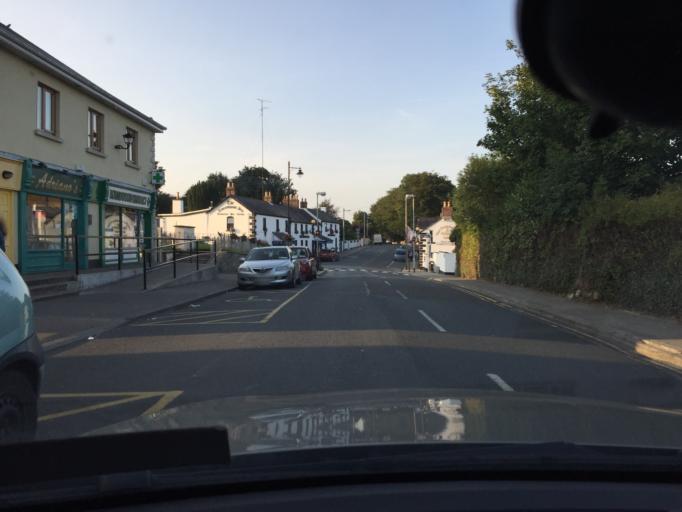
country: IE
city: Newtownmountkennedy
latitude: 53.0638
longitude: -6.2247
